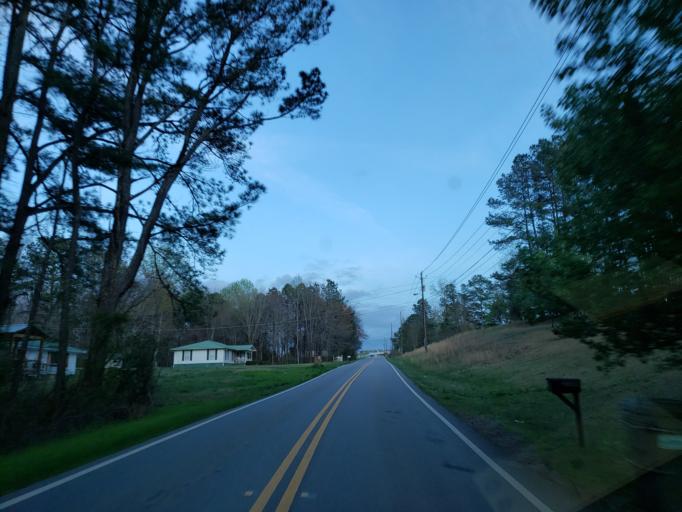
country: US
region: Georgia
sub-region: Polk County
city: Rockmart
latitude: 33.9900
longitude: -84.9660
